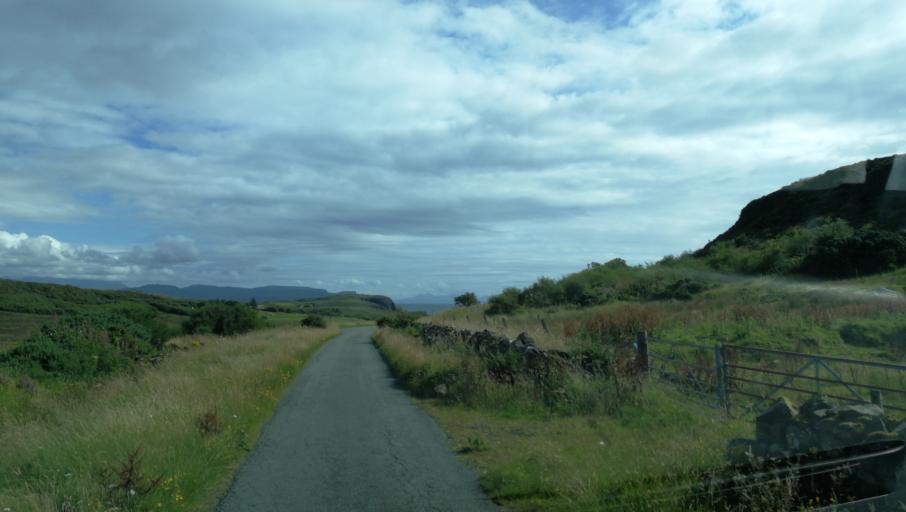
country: GB
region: Scotland
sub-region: Highland
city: Isle of Skye
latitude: 57.4034
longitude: -6.5680
